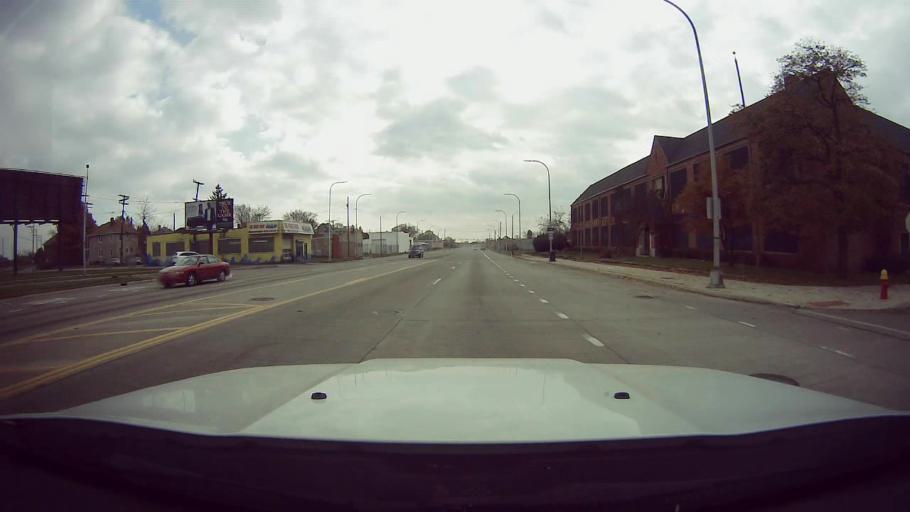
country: US
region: Michigan
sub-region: Wayne County
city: Highland Park
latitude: 42.3666
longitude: -83.1388
